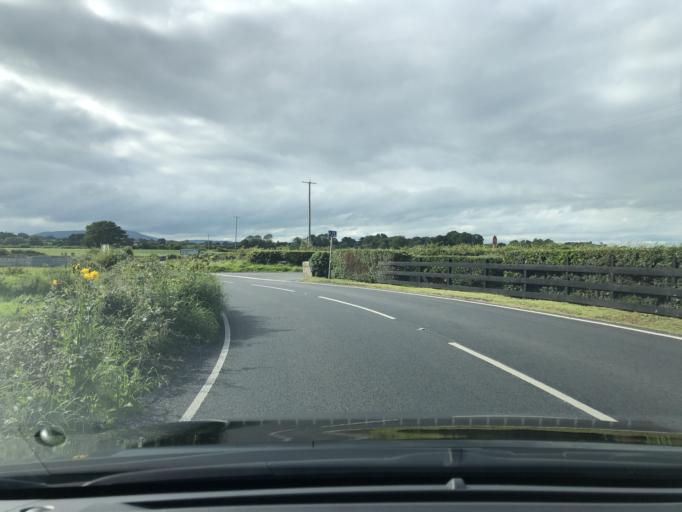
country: GB
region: Northern Ireland
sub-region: Down District
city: Dundrum
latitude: 54.2859
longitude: -5.8123
